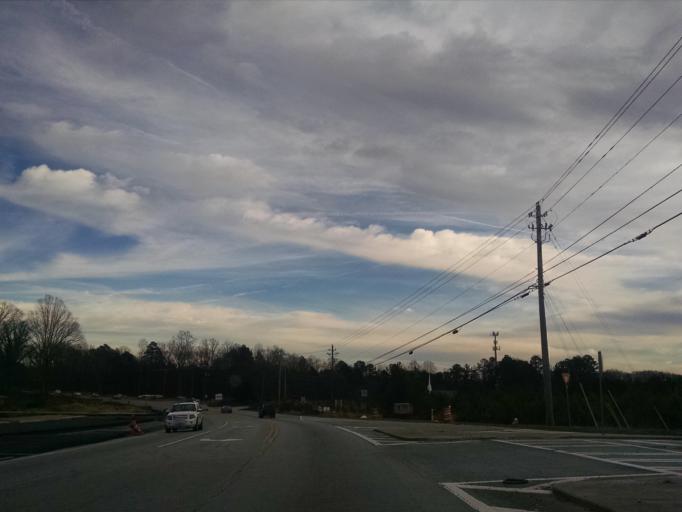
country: US
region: Georgia
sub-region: Gwinnett County
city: Sugar Hill
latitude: 34.1129
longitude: -84.0727
